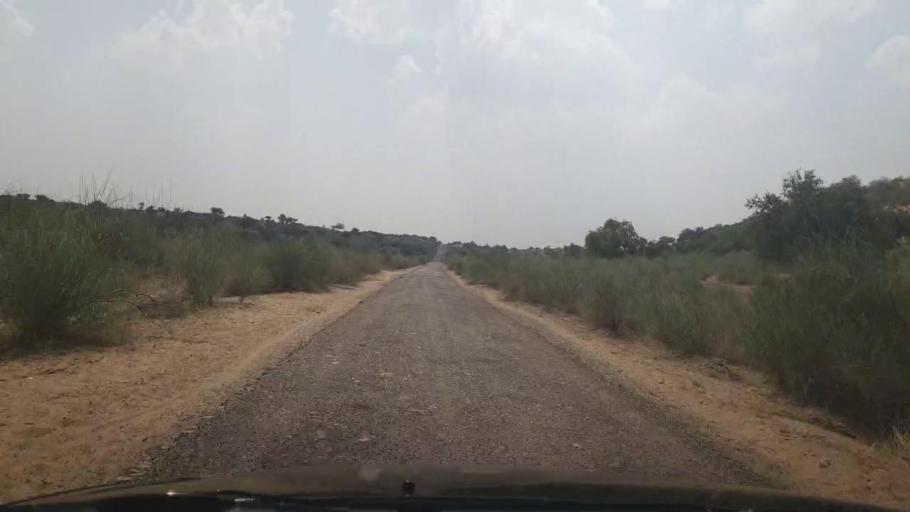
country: PK
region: Sindh
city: Islamkot
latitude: 25.0056
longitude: 70.5022
